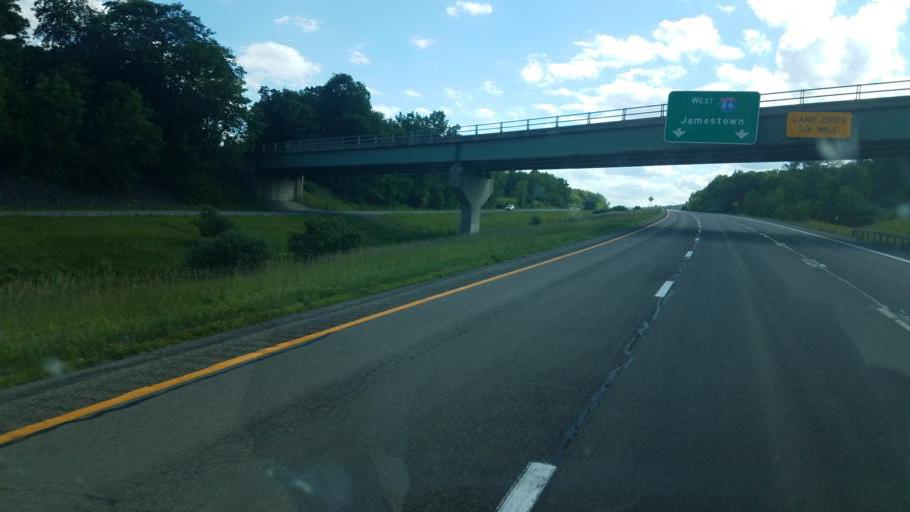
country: US
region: New York
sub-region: Steuben County
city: Hornell
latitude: 42.3642
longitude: -77.6995
